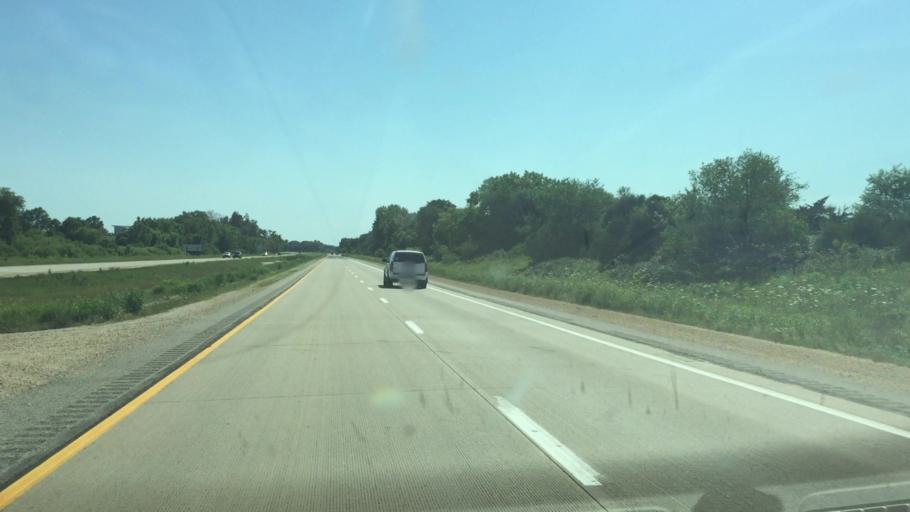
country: US
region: Iowa
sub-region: Jones County
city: Monticello
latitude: 42.2045
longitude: -91.2024
